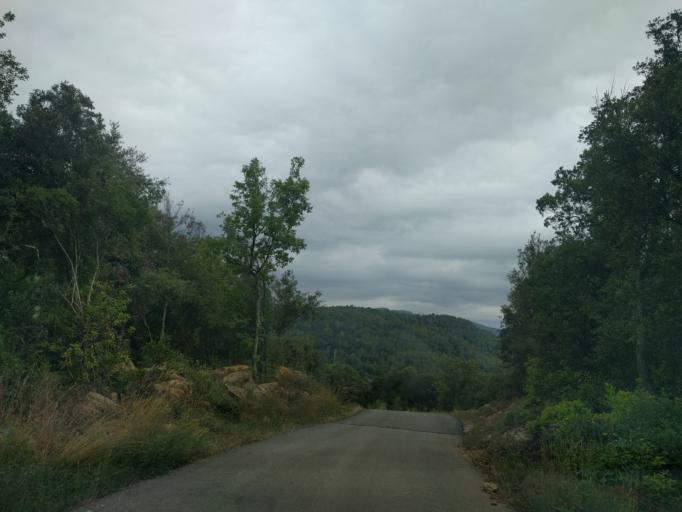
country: ES
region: Catalonia
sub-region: Provincia de Girona
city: la Cellera de Ter
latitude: 42.0339
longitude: 2.6250
